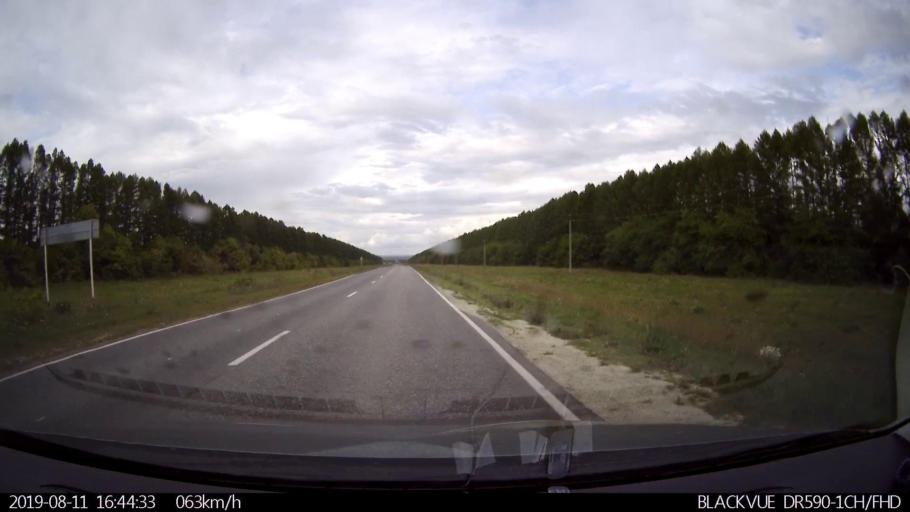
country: RU
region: Ulyanovsk
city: Mayna
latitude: 54.1800
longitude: 47.6805
